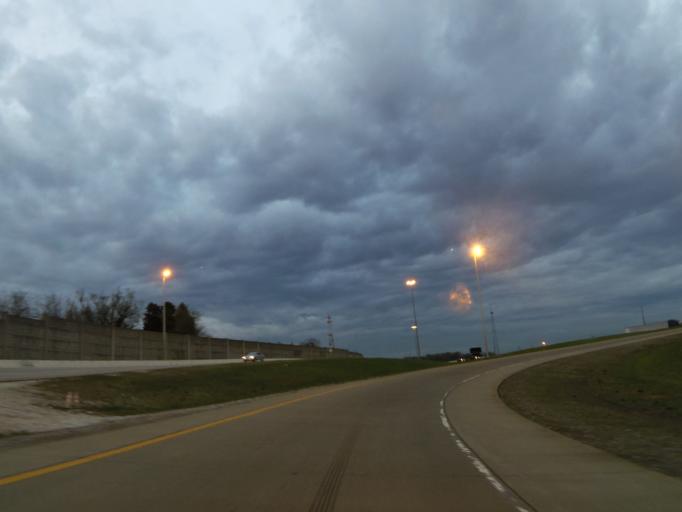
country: US
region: Tennessee
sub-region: Blount County
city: Louisville
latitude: 35.9307
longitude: -84.0414
